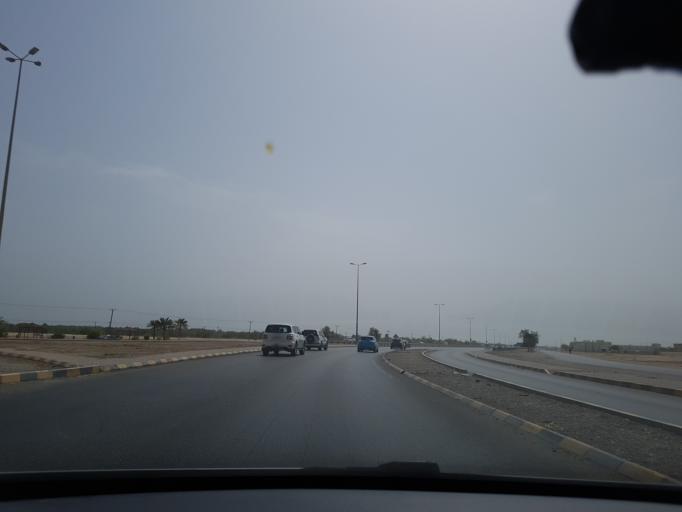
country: OM
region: Al Batinah
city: As Suwayq
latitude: 23.8238
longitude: 57.4244
